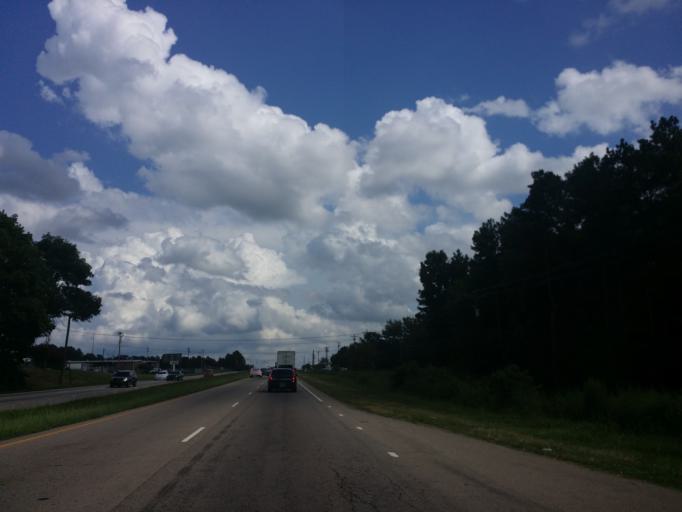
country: US
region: North Carolina
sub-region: Durham County
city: Gorman
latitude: 35.9347
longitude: -78.8126
